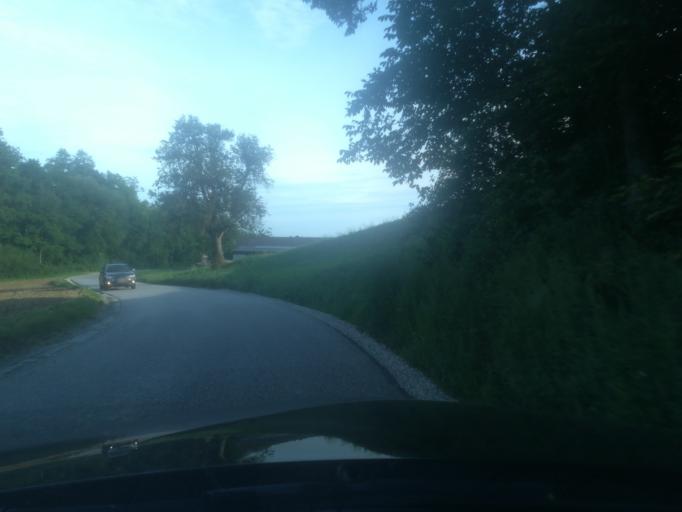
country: AT
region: Upper Austria
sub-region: Wels-Land
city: Marchtrenk
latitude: 48.1731
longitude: 14.1639
